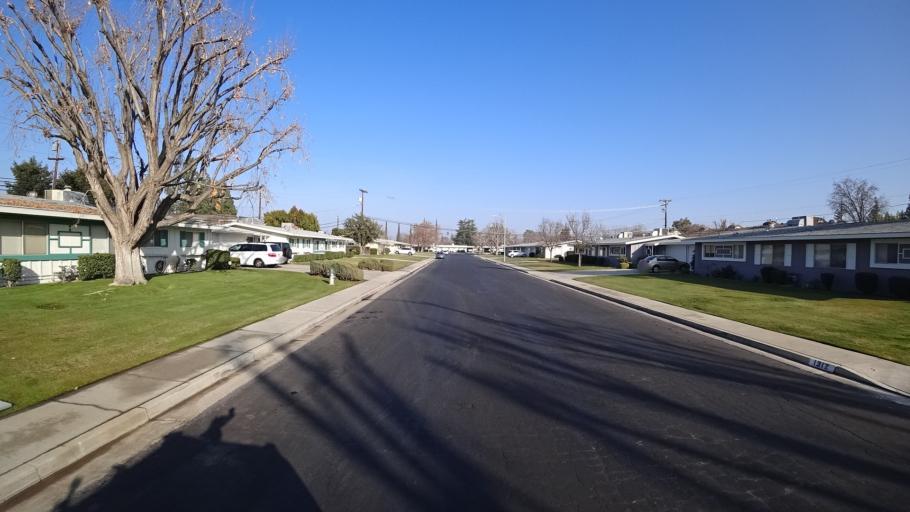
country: US
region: California
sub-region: Kern County
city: Bakersfield
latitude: 35.3428
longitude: -119.0633
